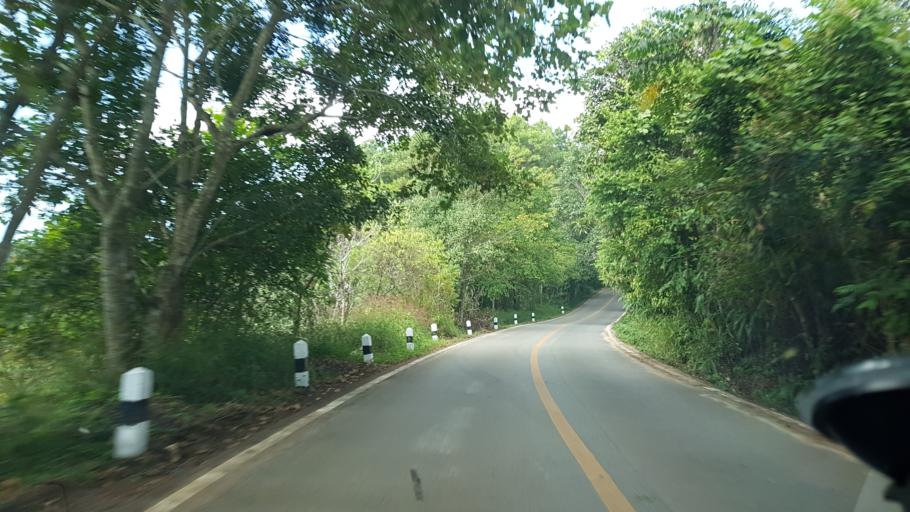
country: TH
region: Chiang Rai
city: Mae Fa Luang
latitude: 20.3285
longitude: 99.8152
